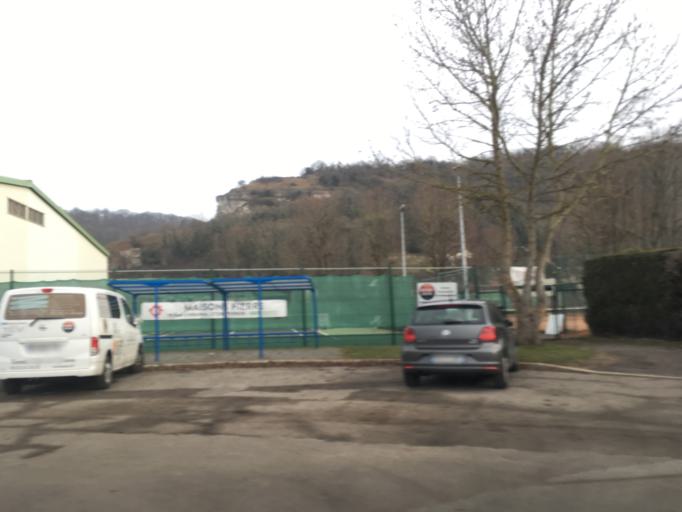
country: FR
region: Haute-Normandie
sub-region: Departement de l'Eure
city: Vernon
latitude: 49.0956
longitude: 1.4918
